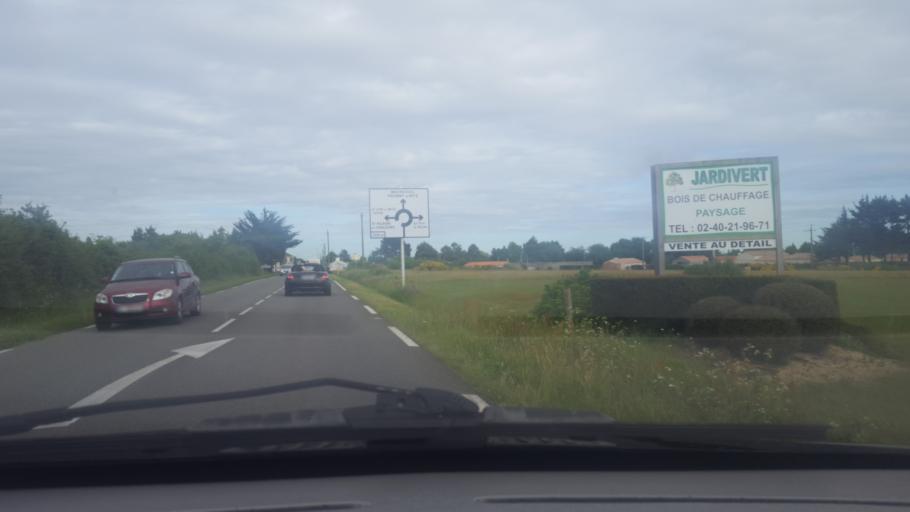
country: FR
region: Pays de la Loire
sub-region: Departement de la Loire-Atlantique
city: Bourgneuf-en-Retz
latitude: 47.0302
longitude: -1.9082
